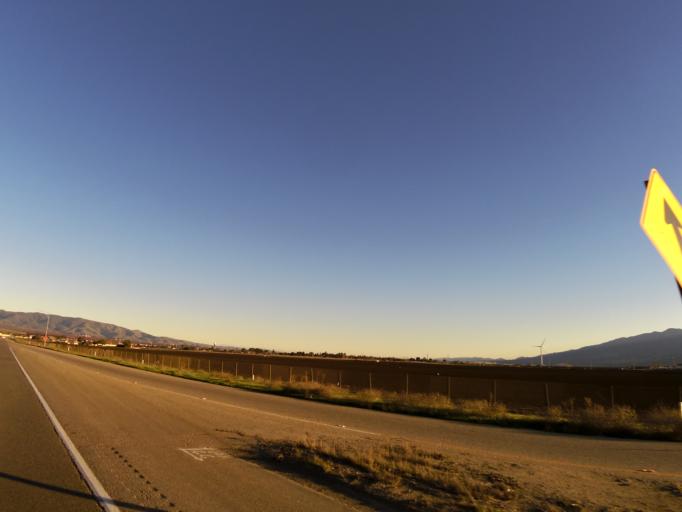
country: US
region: California
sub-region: Monterey County
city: Gonzales
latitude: 36.5229
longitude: -121.4613
